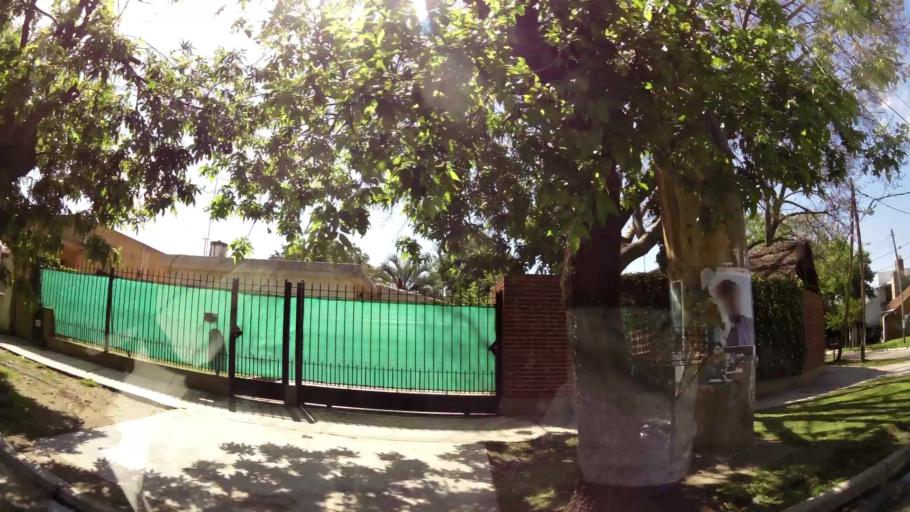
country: AR
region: Buenos Aires
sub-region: Partido de Quilmes
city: Quilmes
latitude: -34.8182
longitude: -58.2759
